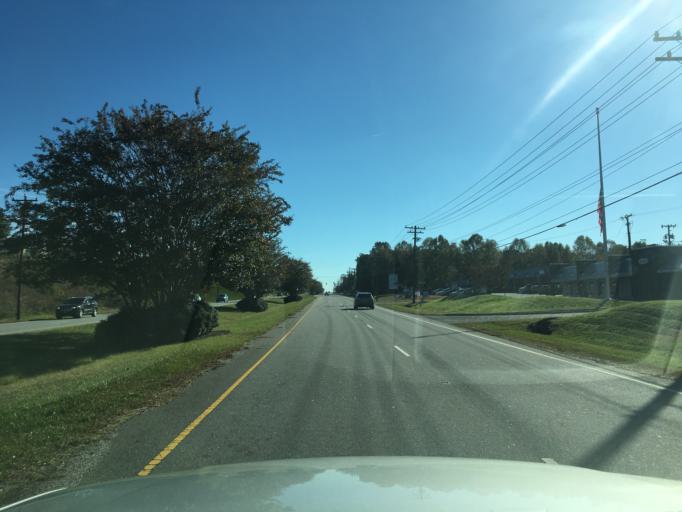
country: US
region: North Carolina
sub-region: Catawba County
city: Hickory
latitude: 35.7293
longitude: -81.3124
